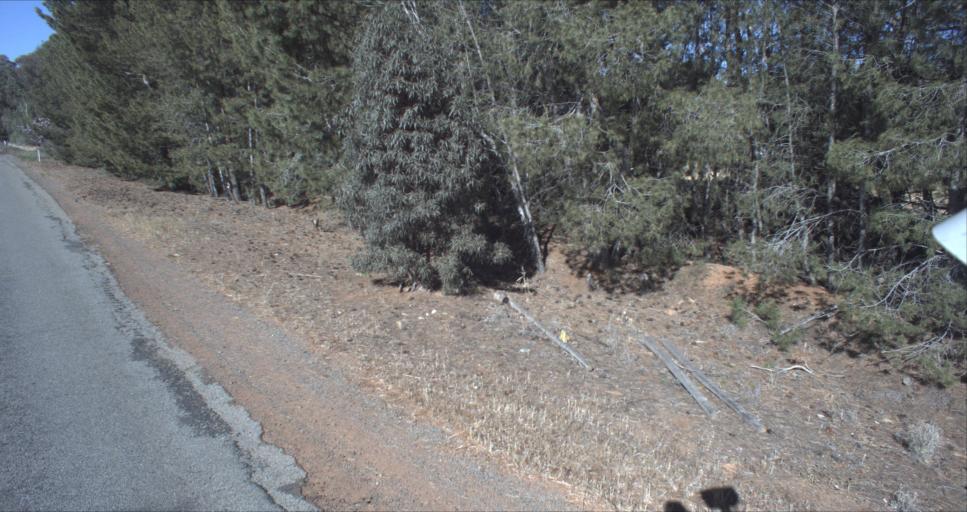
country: AU
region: New South Wales
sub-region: Leeton
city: Leeton
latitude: -34.5720
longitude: 146.3104
